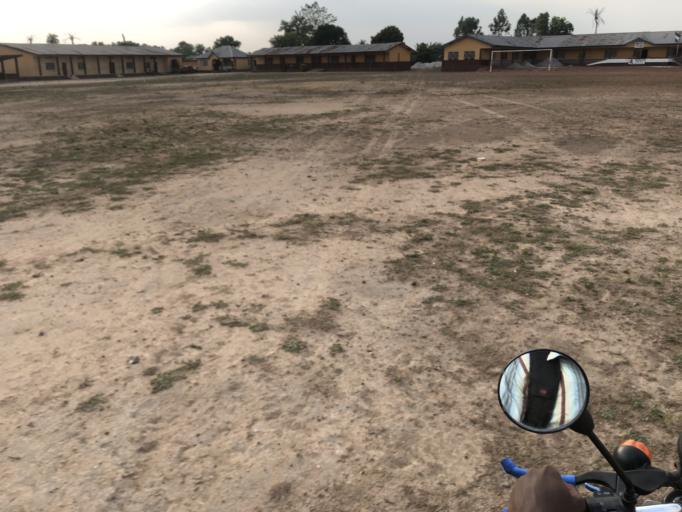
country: SL
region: Northern Province
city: Yonibana
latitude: 8.4694
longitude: -12.2038
